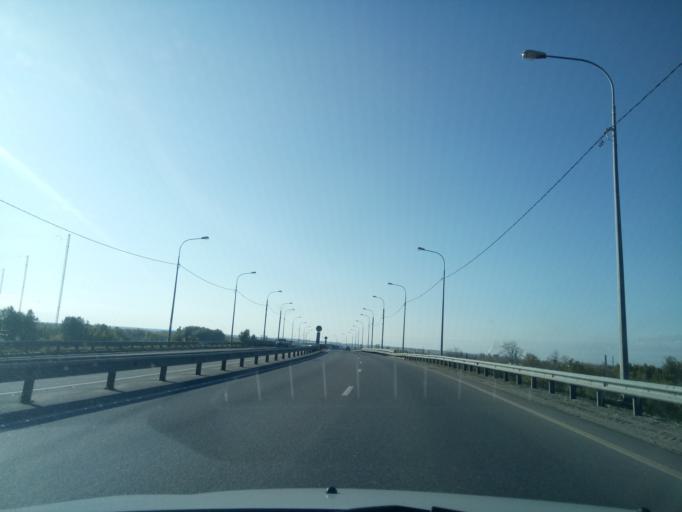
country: RU
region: Nizjnij Novgorod
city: Burevestnik
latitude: 56.1796
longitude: 43.9134
